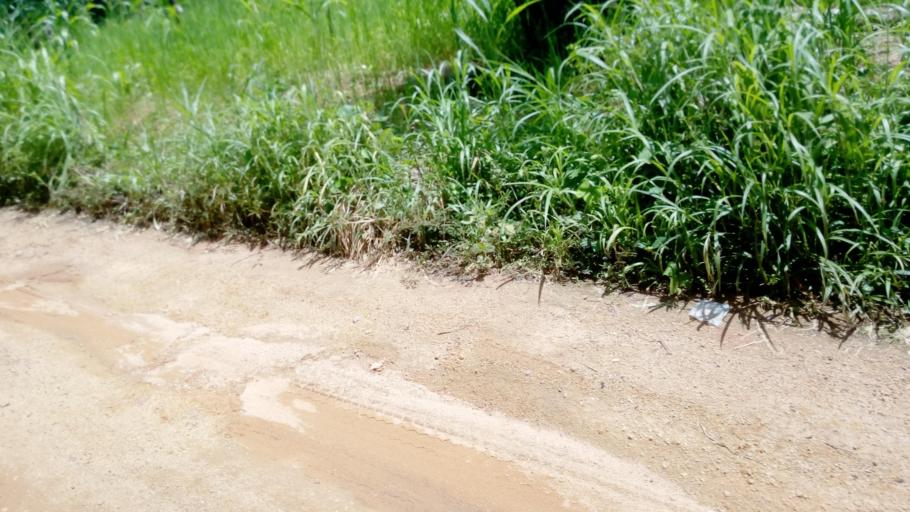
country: SL
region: Northern Province
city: Binkolo
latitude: 8.9543
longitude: -11.9690
